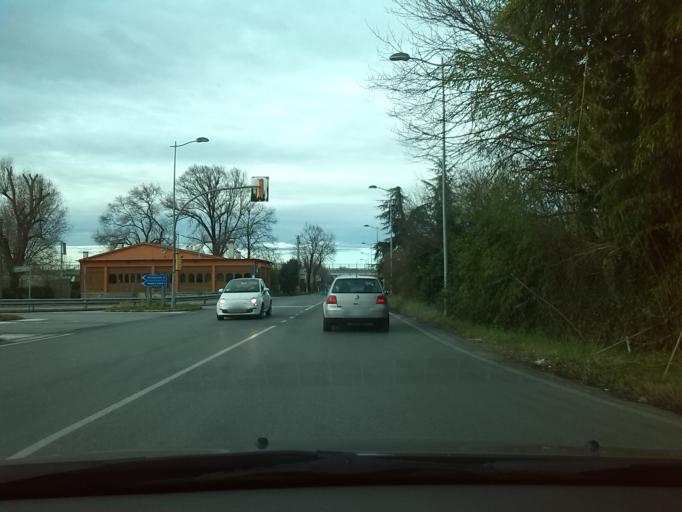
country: IT
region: Friuli Venezia Giulia
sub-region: Provincia di Gorizia
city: Sagrado
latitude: 45.8921
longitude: 13.4767
